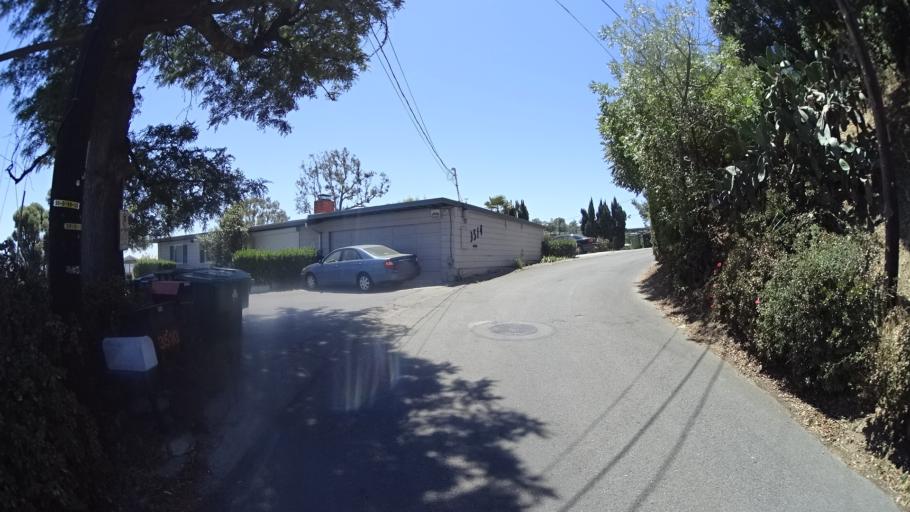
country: US
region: California
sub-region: Los Angeles County
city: Universal City
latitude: 34.1283
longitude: -118.3597
